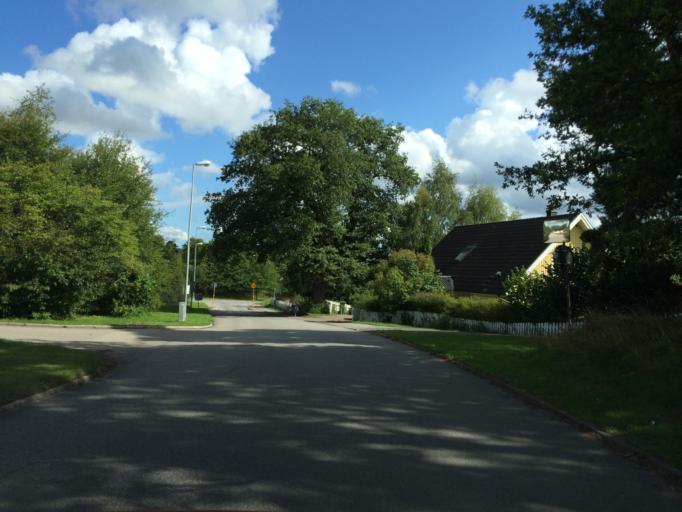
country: SE
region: Stockholm
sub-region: Sollentuna Kommun
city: Sollentuna
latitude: 59.4613
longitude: 17.9080
